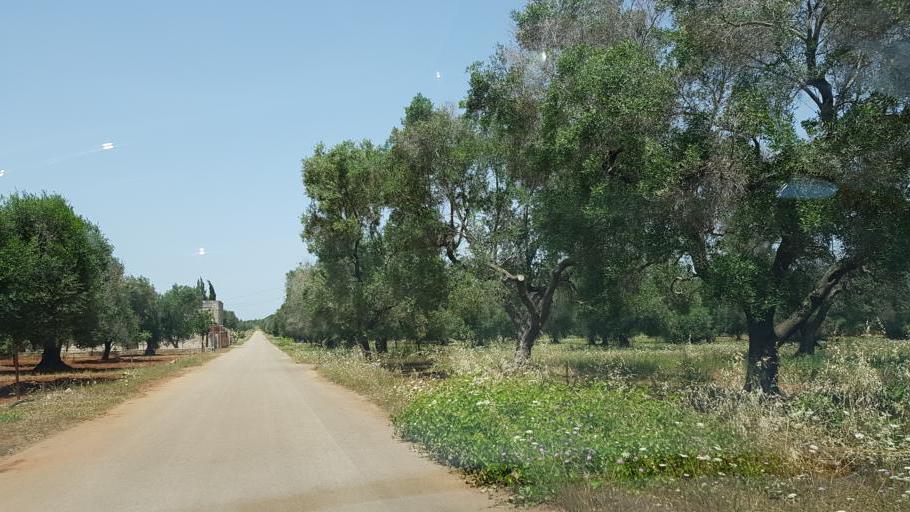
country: IT
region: Apulia
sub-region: Provincia di Lecce
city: Porto Cesareo
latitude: 40.3188
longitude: 17.8948
